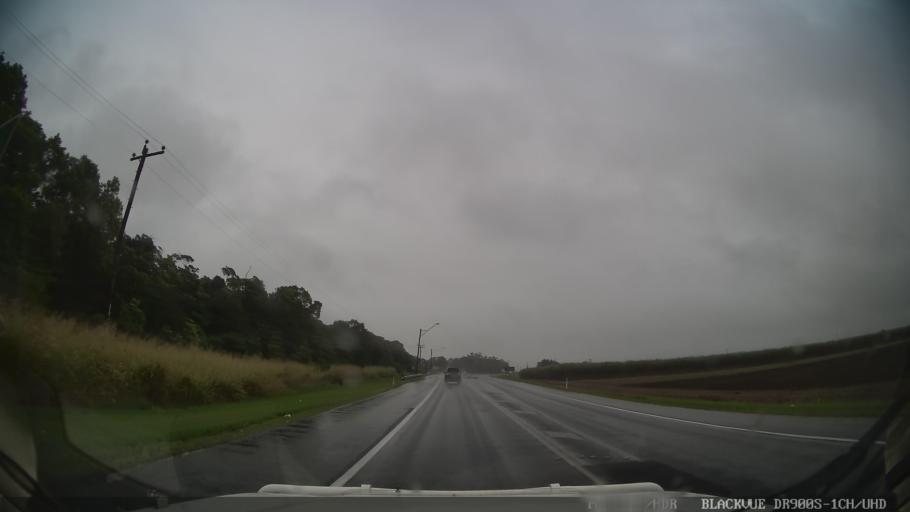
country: AU
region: Queensland
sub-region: Cassowary Coast
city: Innisfail
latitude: -17.7508
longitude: 146.0277
